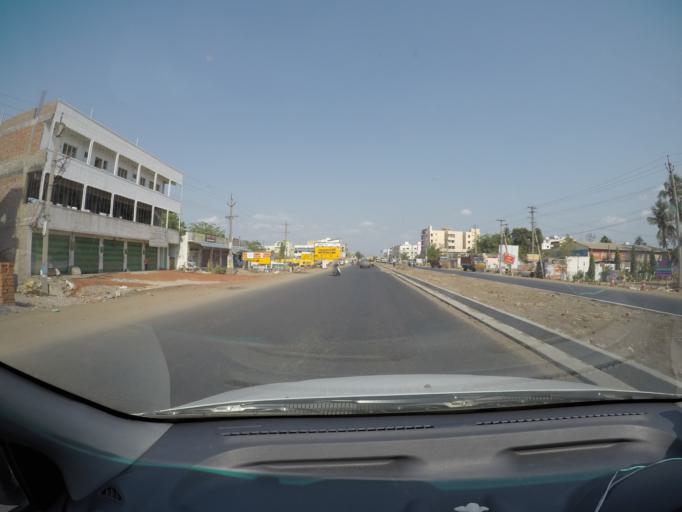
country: IN
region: Andhra Pradesh
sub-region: Krishna
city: Yanamalakuduru
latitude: 16.4782
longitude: 80.7018
